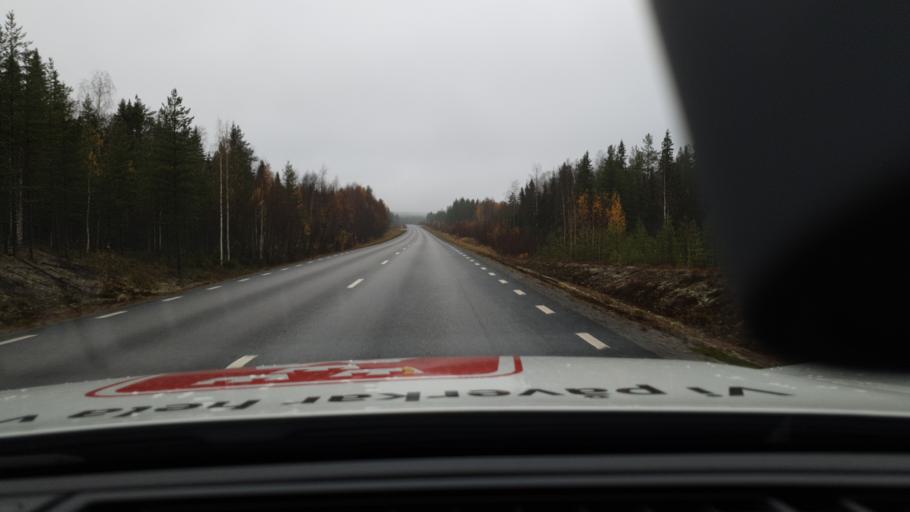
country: SE
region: Norrbotten
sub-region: Overkalix Kommun
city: OEverkalix
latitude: 66.6246
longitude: 22.2230
